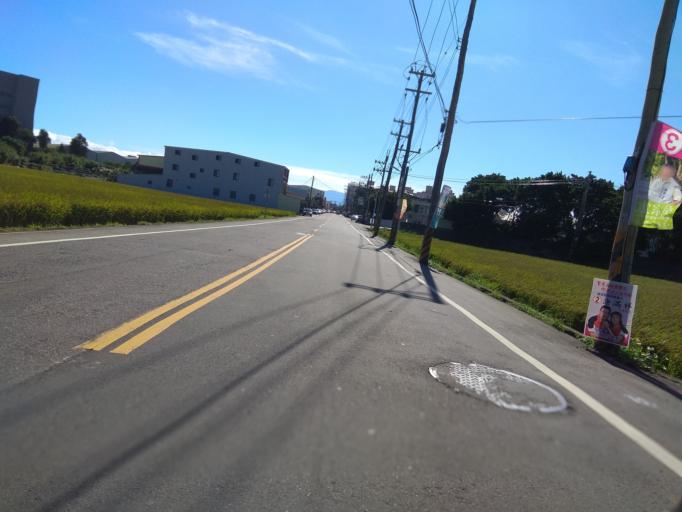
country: TW
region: Taiwan
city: Taoyuan City
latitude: 24.9770
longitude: 121.1366
